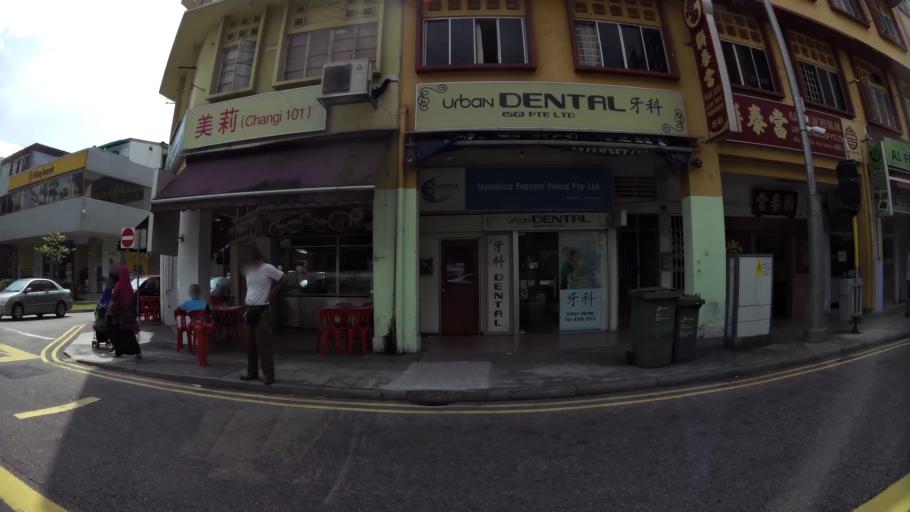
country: SG
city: Singapore
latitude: 1.3164
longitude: 103.8994
